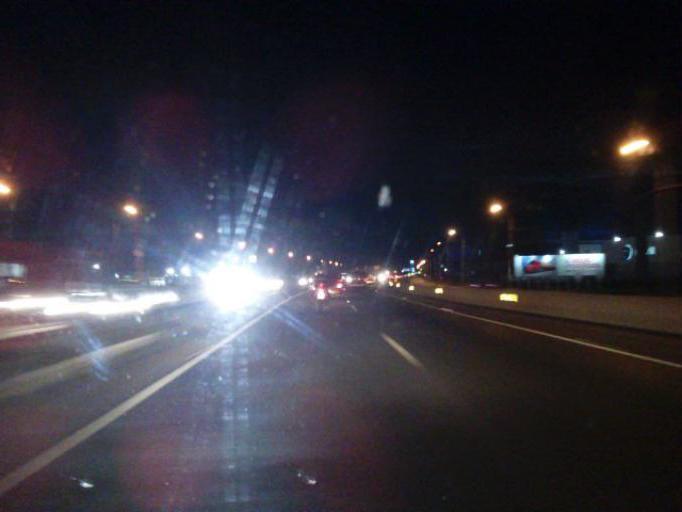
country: BR
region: Santa Catarina
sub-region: Itajai
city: Itajai
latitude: -26.8592
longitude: -48.7278
